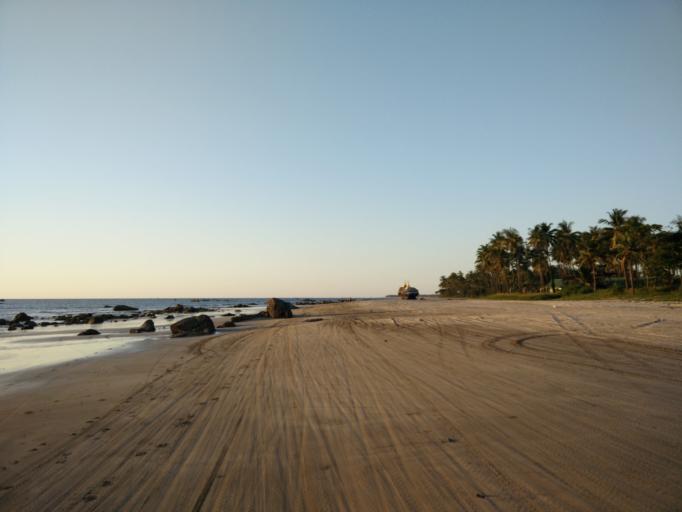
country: MM
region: Ayeyarwady
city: Pathein
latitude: 16.8326
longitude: 94.3936
